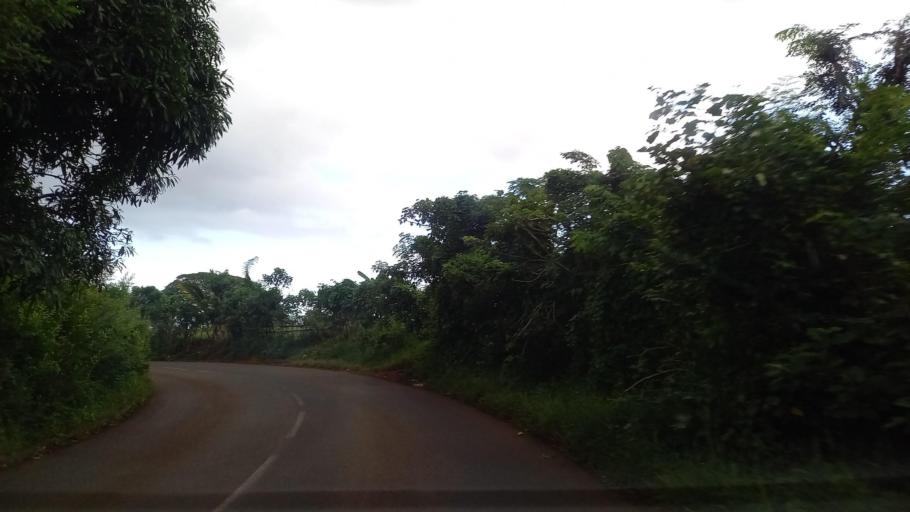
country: YT
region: Tsingoni
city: Tsingoni
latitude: -12.7842
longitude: 45.1420
